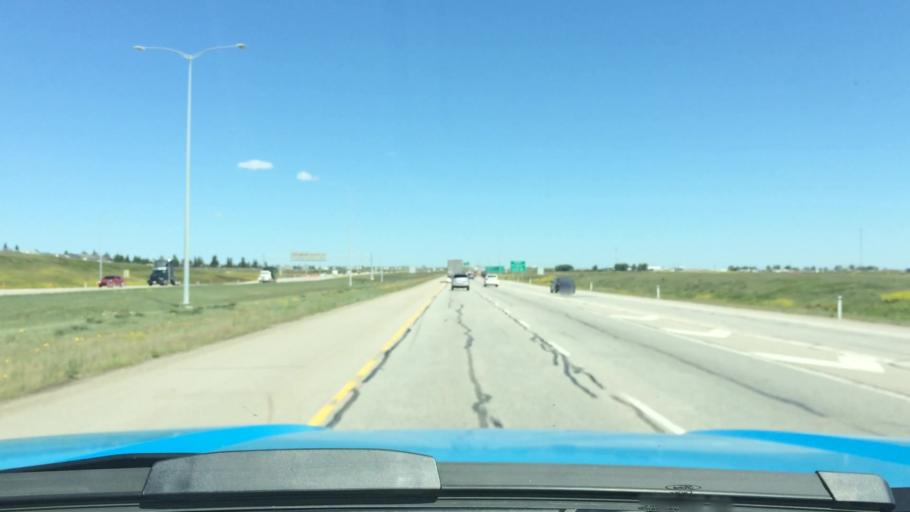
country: CA
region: Alberta
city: Chestermere
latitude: 51.0723
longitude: -113.9202
